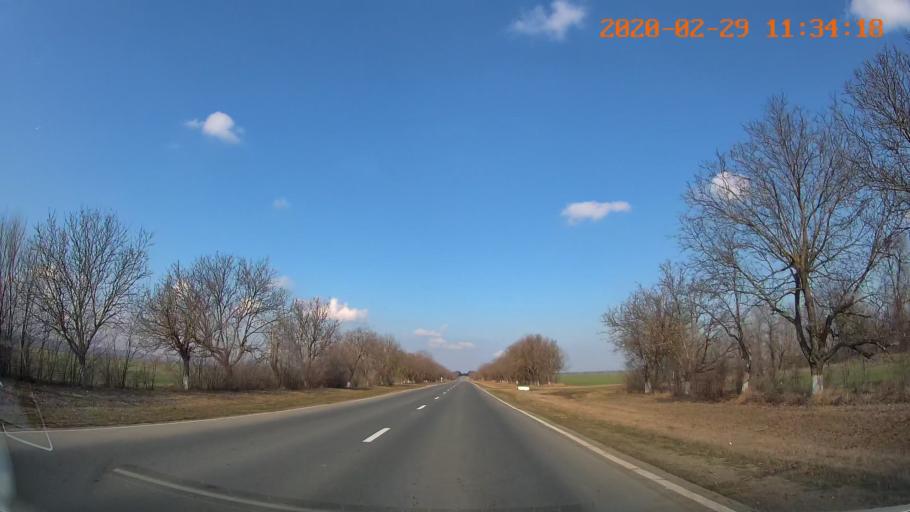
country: MD
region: Rezina
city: Saharna
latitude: 47.5637
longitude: 29.0753
